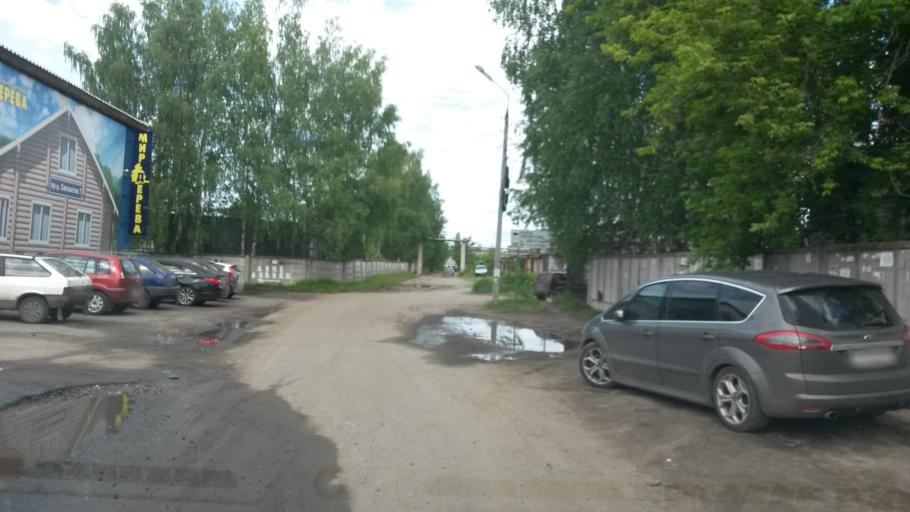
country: RU
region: Jaroslavl
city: Yaroslavl
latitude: 57.6495
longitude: 39.9124
